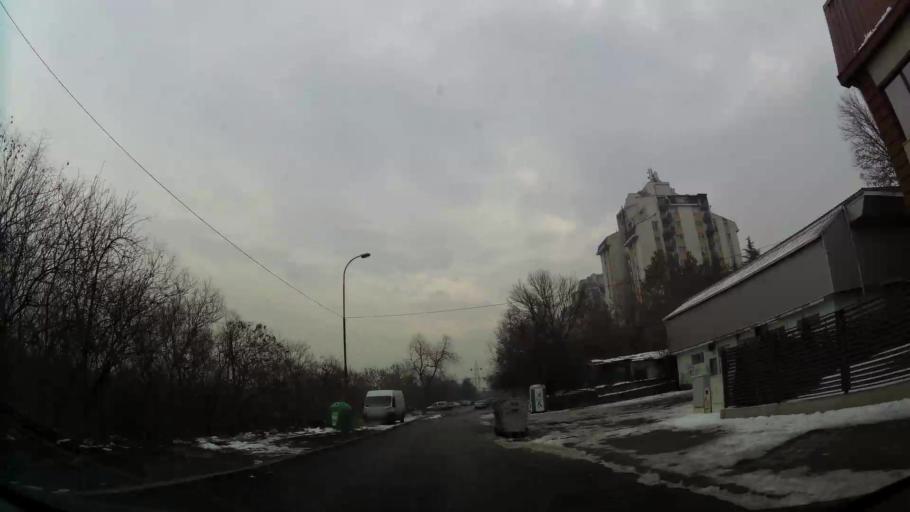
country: MK
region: Cair
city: Cair
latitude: 42.0112
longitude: 21.4611
